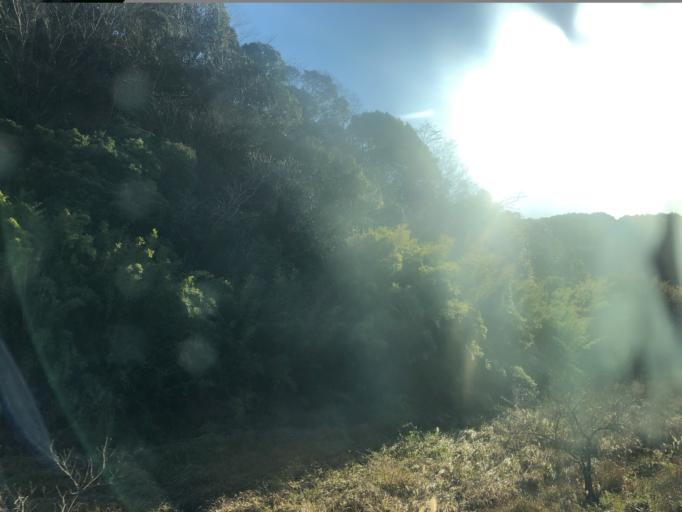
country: JP
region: Kochi
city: Nakamura
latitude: 33.0093
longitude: 132.9879
